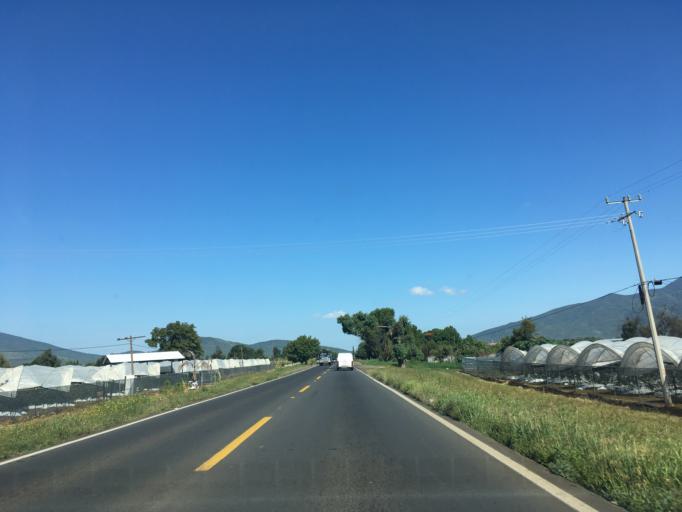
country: MX
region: Mexico
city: Tangancicuaro de Arista
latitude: 19.8680
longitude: -102.1927
